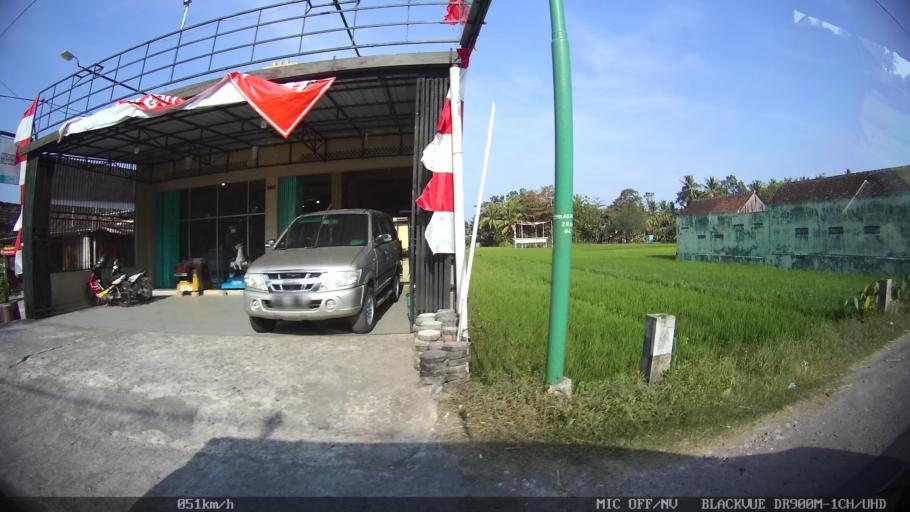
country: ID
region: Daerah Istimewa Yogyakarta
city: Pandak
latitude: -7.8918
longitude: 110.3030
